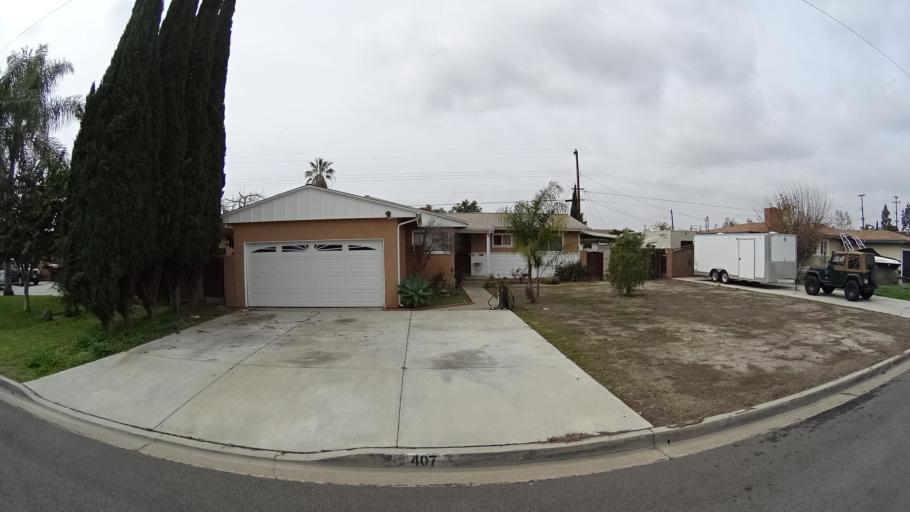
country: US
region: California
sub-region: Orange County
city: Stanton
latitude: 33.8270
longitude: -117.9858
